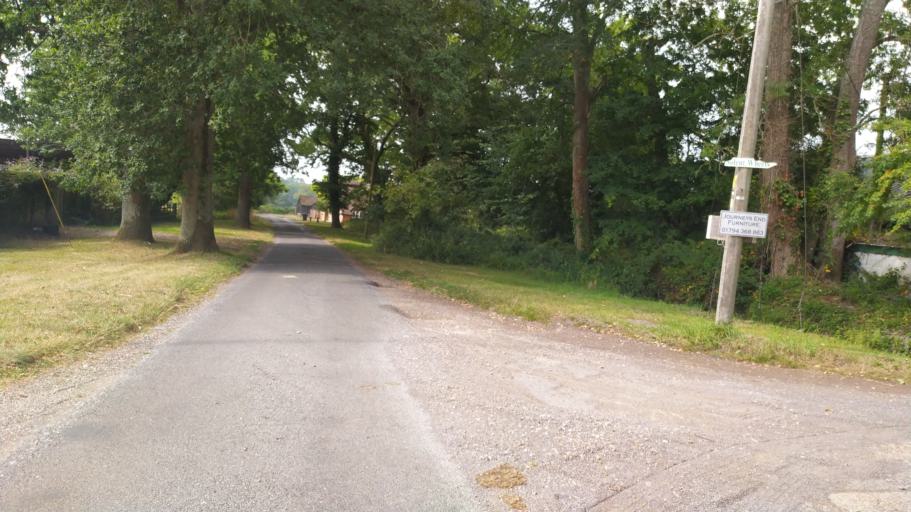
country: GB
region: England
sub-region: Hampshire
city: Romsey
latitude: 51.0006
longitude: -1.4418
